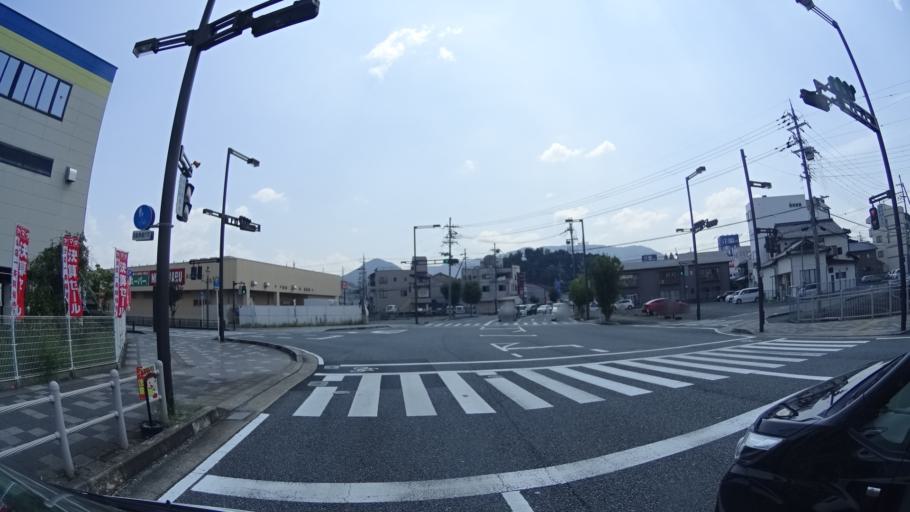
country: JP
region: Kyoto
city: Fukuchiyama
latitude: 35.2967
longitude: 135.1154
